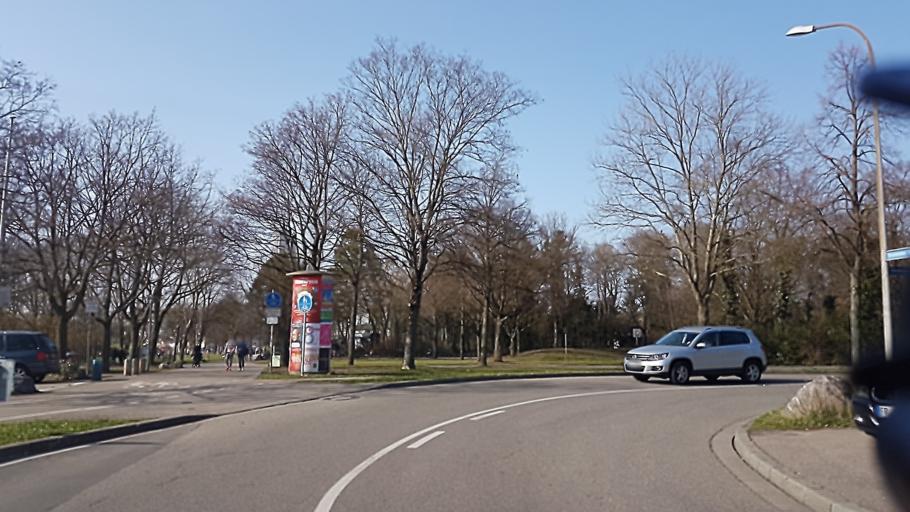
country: DE
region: Baden-Wuerttemberg
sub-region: Freiburg Region
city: Freiburg
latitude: 48.0117
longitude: 7.8227
